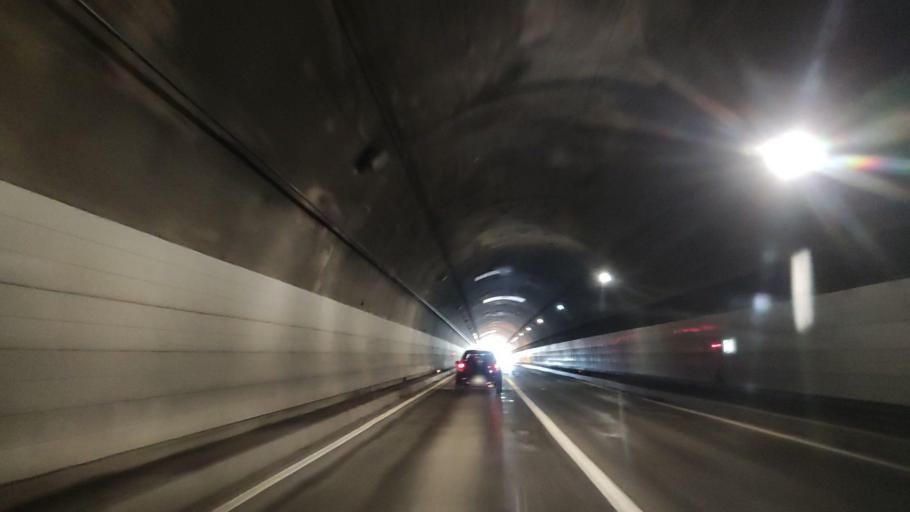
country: JP
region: Akita
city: Takanosu
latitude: 40.2120
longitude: 140.2161
